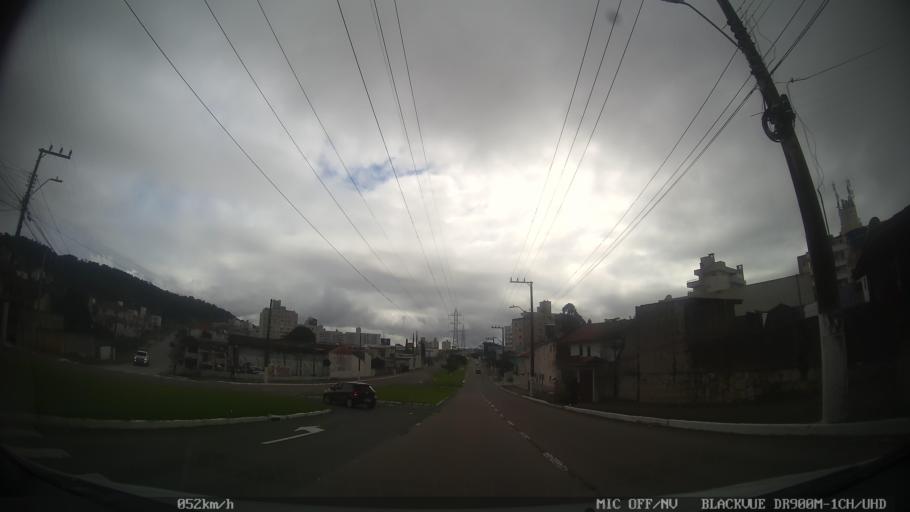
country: BR
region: Santa Catarina
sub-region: Sao Jose
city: Campinas
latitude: -27.5824
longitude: -48.6207
